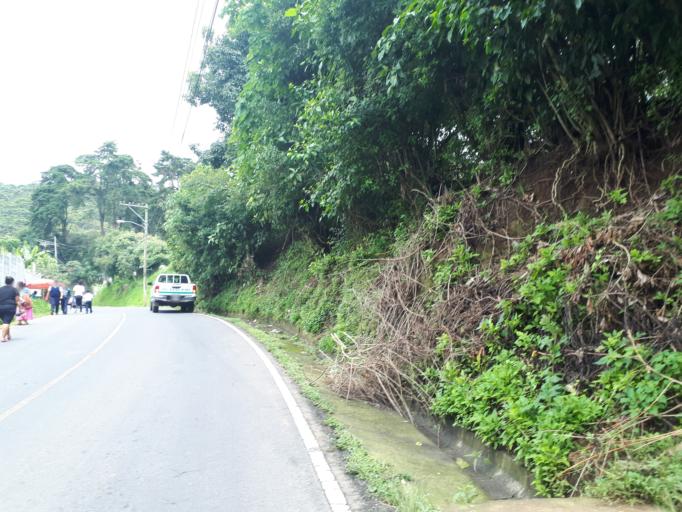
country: GT
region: Guatemala
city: Villa Canales
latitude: 14.4571
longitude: -90.5074
